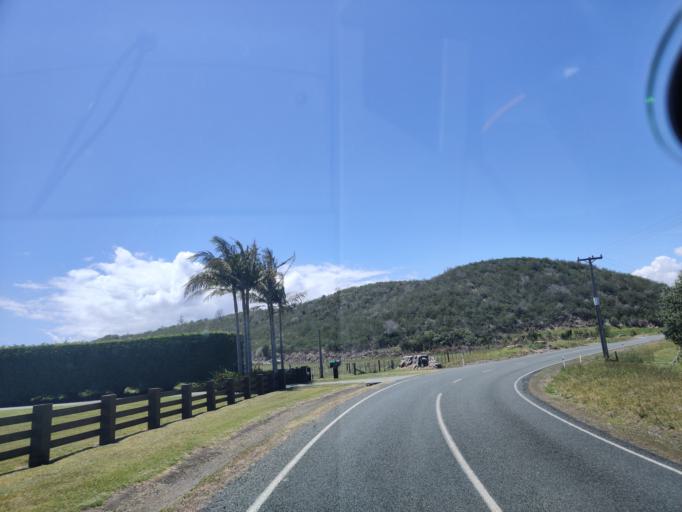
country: NZ
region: Northland
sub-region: Far North District
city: Kaitaia
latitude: -35.0253
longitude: 173.1974
